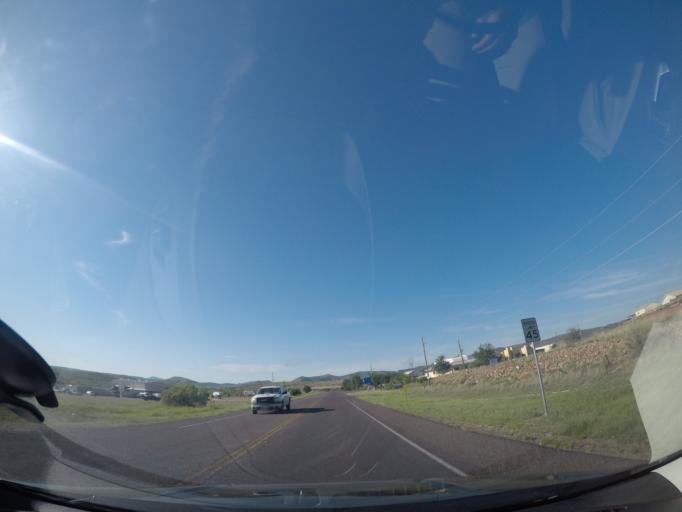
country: US
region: Texas
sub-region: Brewster County
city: Alpine
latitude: 30.3502
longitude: -103.6508
